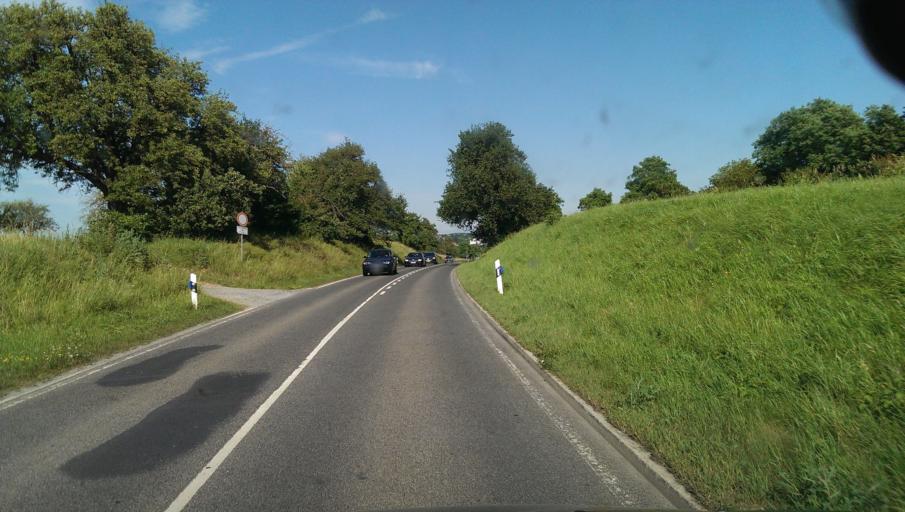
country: DE
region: Baden-Wuerttemberg
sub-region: Regierungsbezirk Stuttgart
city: Ohringen
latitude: 49.1992
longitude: 9.4794
